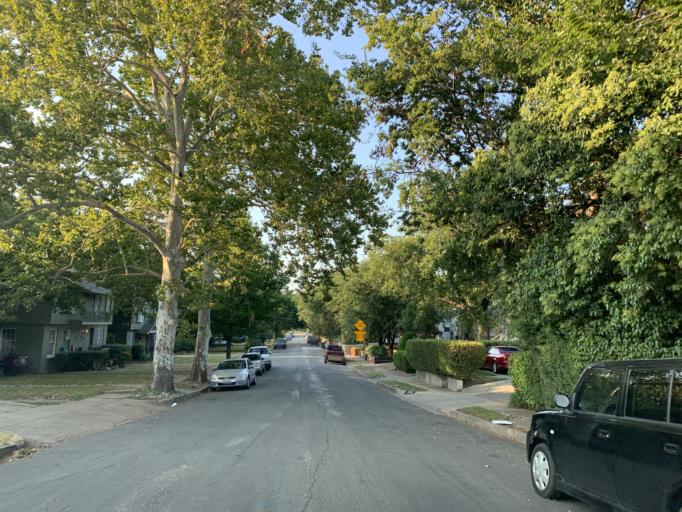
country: US
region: Texas
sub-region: Dallas County
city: Cockrell Hill
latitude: 32.7471
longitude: -96.8527
